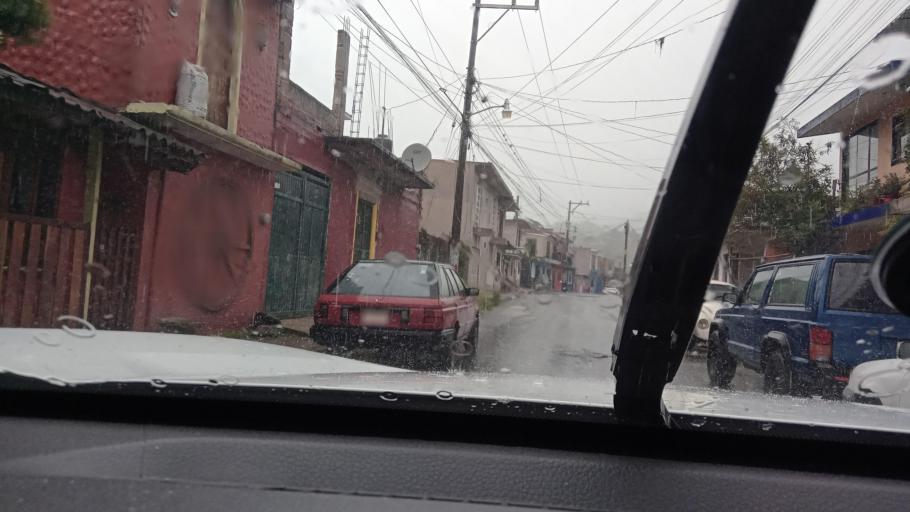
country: MX
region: Veracruz
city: Coatepec
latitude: 19.4603
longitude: -96.9740
